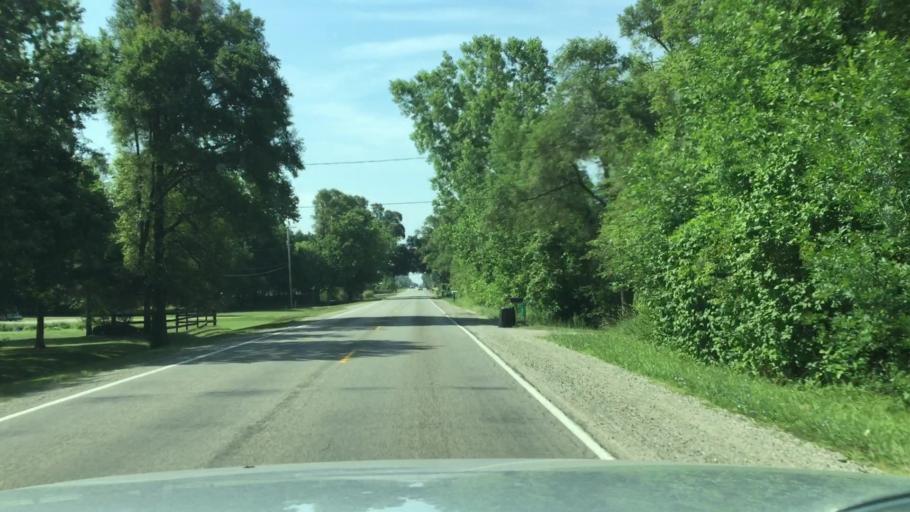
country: US
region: Michigan
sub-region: Genesee County
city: Flushing
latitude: 43.0854
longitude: -83.8135
